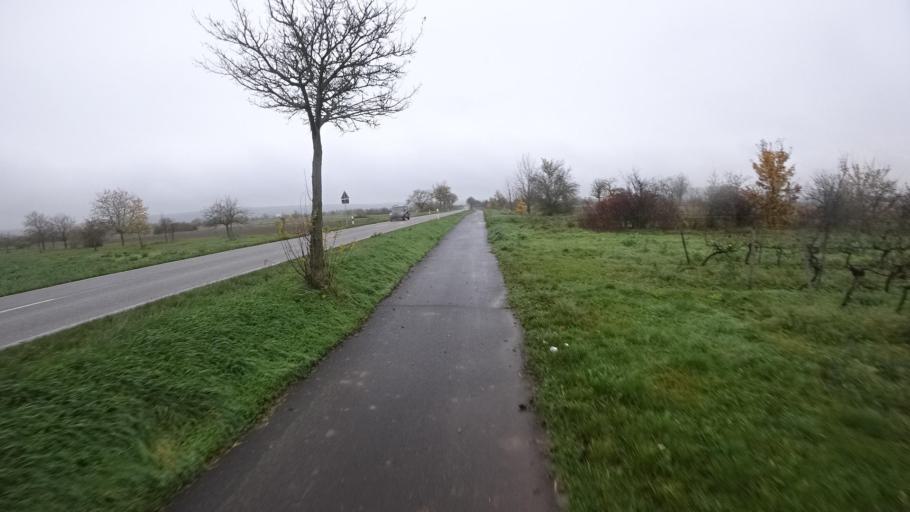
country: DE
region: Rheinland-Pfalz
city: Gimbsheim
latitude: 49.7844
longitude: 8.3701
